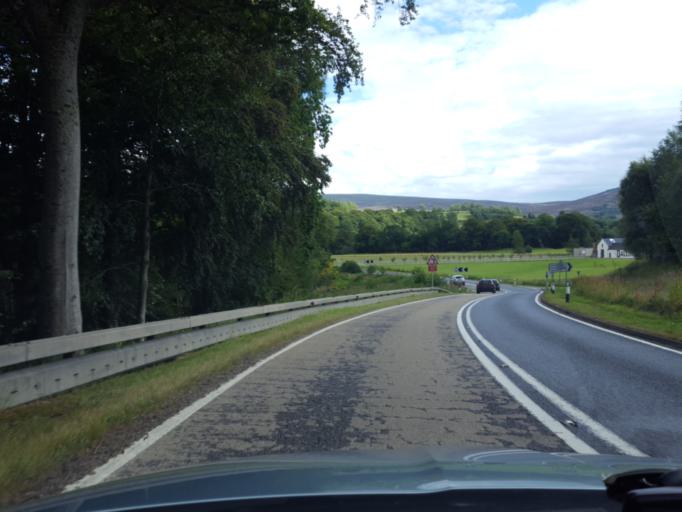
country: GB
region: Scotland
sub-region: Moray
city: Rothes
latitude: 57.4071
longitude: -3.3720
